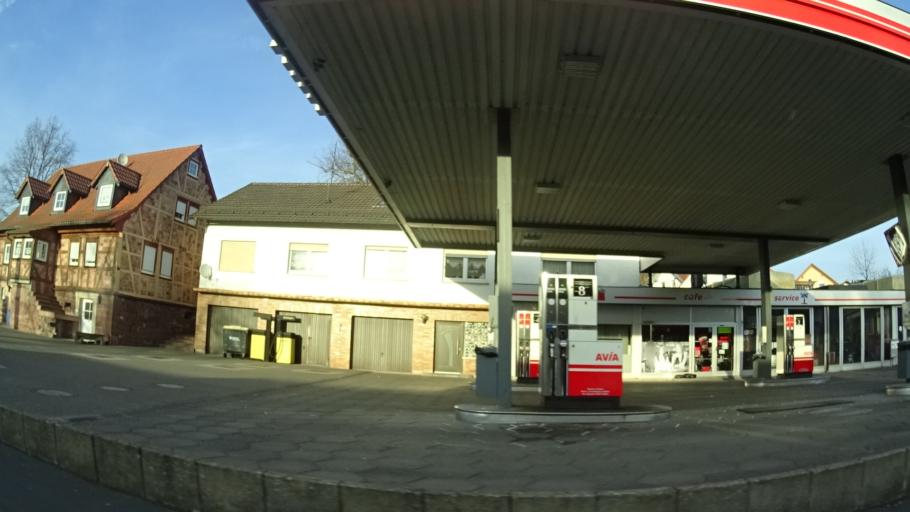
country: DE
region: Bavaria
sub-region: Regierungsbezirk Unterfranken
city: Zeitlofs
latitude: 50.3135
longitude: 9.6204
